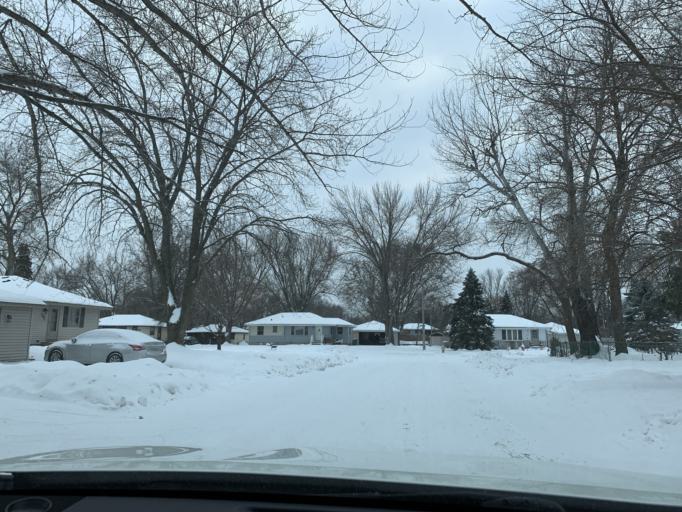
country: US
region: Minnesota
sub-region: Anoka County
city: Coon Rapids
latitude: 45.1724
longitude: -93.2862
